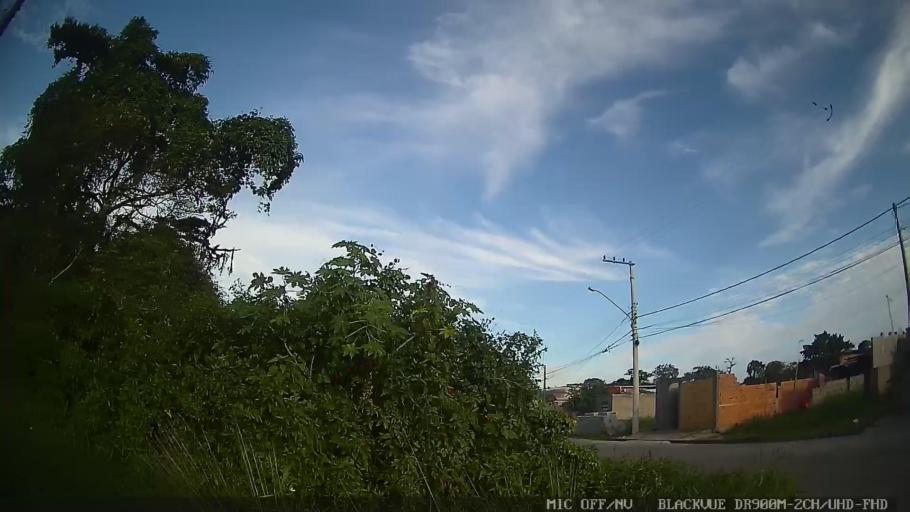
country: BR
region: Sao Paulo
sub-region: Itanhaem
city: Itanhaem
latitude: -24.1554
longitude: -46.7783
